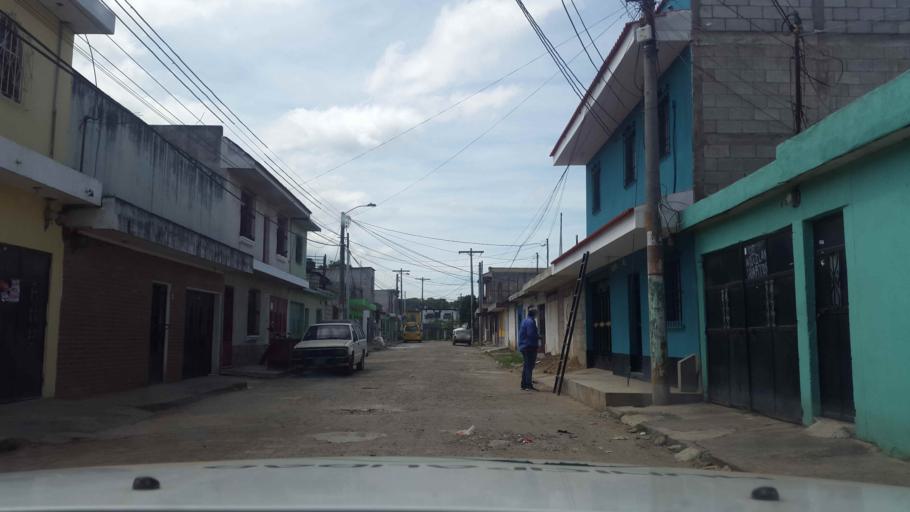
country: GT
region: Guatemala
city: Petapa
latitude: 14.5007
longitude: -90.5676
